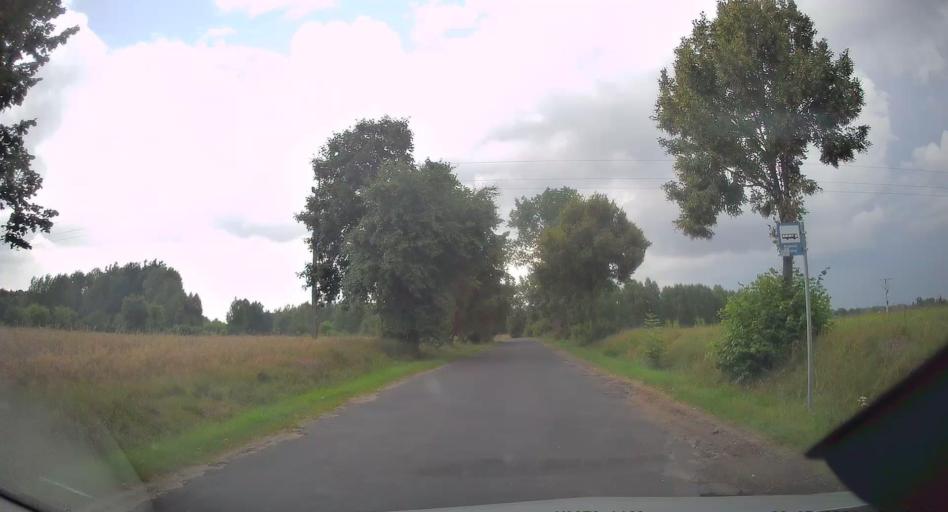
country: PL
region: Lodz Voivodeship
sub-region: Powiat rawski
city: Rawa Mazowiecka
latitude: 51.7405
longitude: 20.1897
